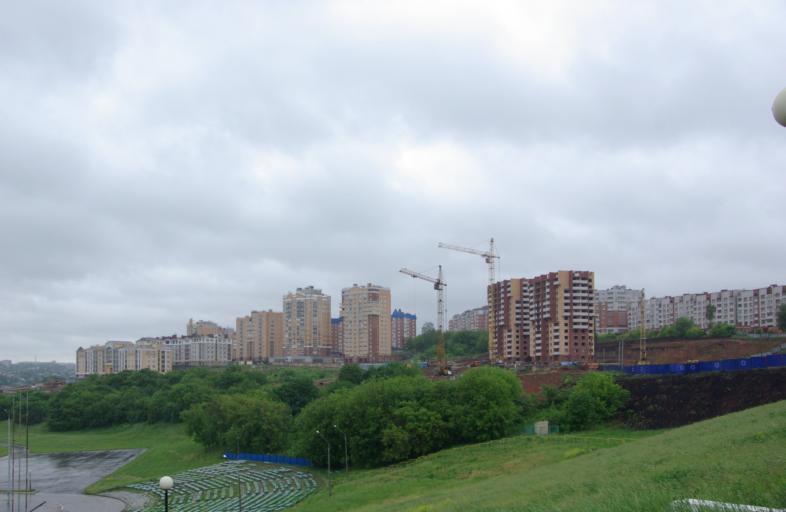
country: RU
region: Chuvashia
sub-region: Cheboksarskiy Rayon
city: Cheboksary
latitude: 56.1521
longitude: 47.2441
